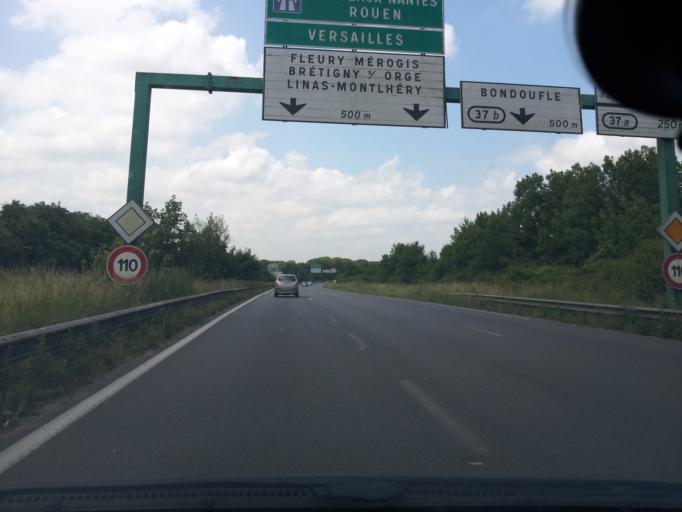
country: FR
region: Ile-de-France
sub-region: Departement de l'Essonne
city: Courcouronnes
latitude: 48.6261
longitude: 2.3968
